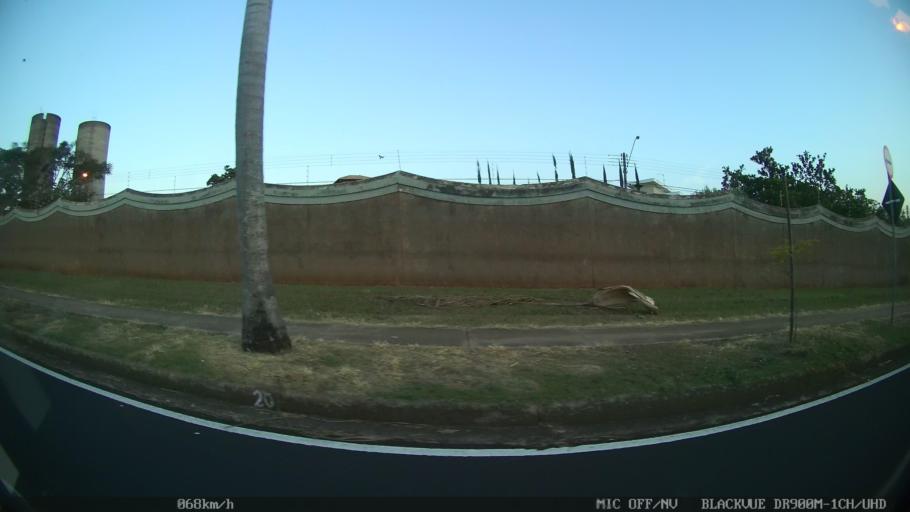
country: BR
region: Sao Paulo
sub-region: Sao Jose Do Rio Preto
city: Sao Jose do Rio Preto
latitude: -20.8171
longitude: -49.3403
